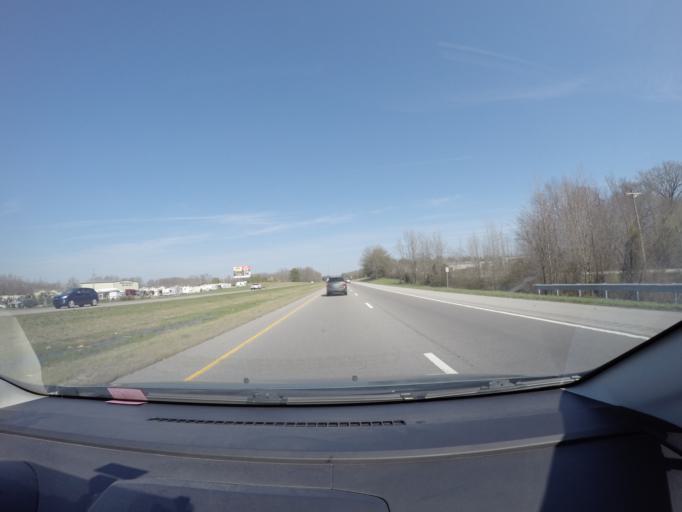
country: US
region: Tennessee
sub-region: Coffee County
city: Manchester
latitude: 35.4635
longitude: -86.0546
